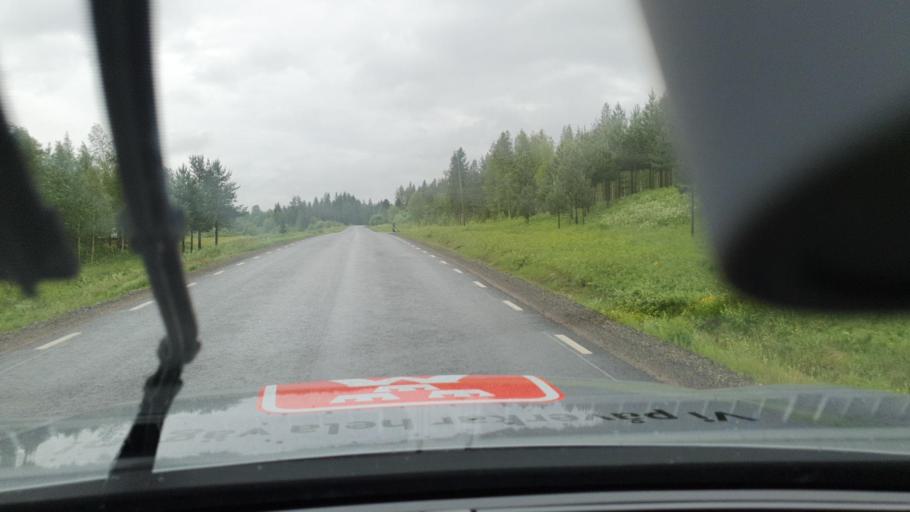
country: FI
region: Lapland
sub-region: Torniolaakso
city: Ylitornio
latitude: 66.2081
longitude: 23.6965
